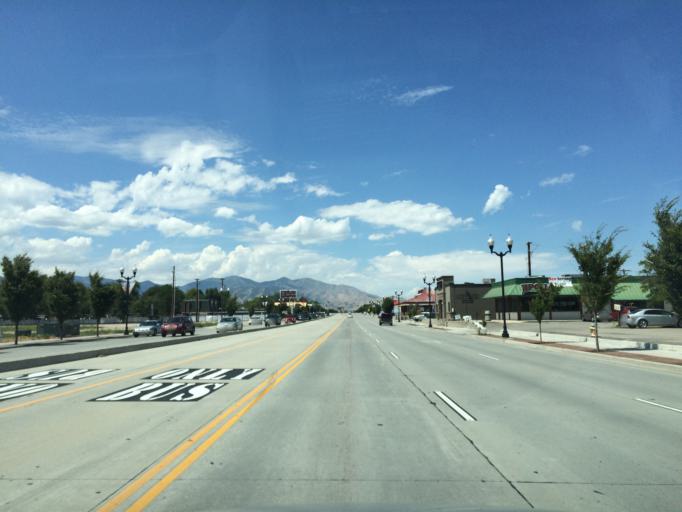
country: US
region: Utah
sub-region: Salt Lake County
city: Taylorsville
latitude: 40.6967
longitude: -111.9619
